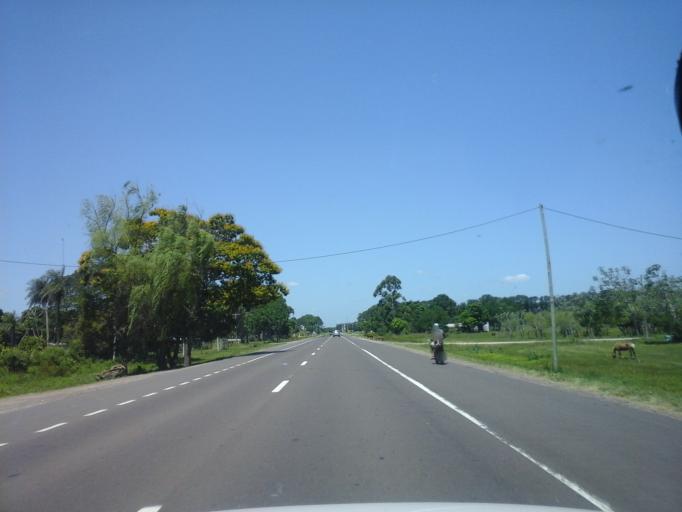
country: AR
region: Corrientes
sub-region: Departamento de San Cosme
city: San Cosme
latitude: -27.3745
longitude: -58.4907
